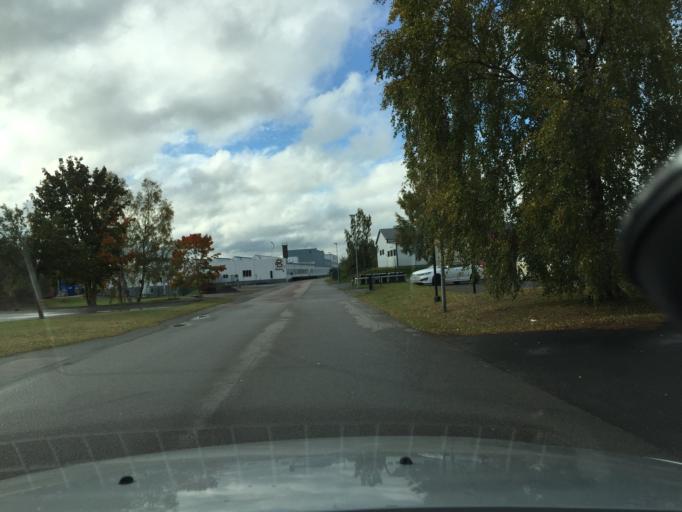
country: SE
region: Skane
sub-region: Hassleholms Kommun
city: Sosdala
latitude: 56.0421
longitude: 13.6883
